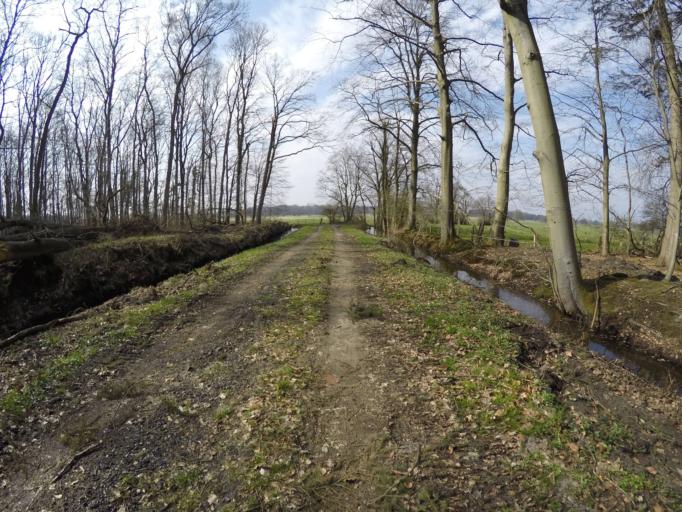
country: DE
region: Schleswig-Holstein
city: Borstel-Hohenraden
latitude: 53.7254
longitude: 9.8213
